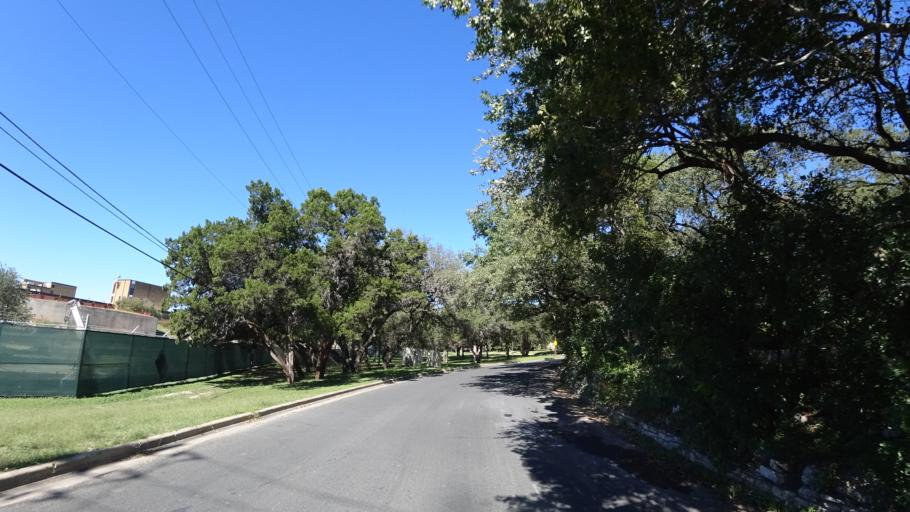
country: US
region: Texas
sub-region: Travis County
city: West Lake Hills
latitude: 30.3149
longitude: -97.7695
